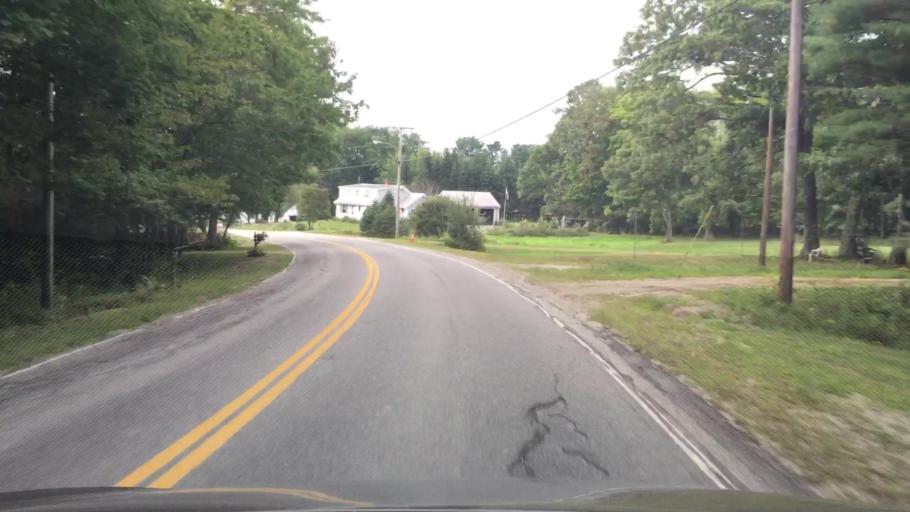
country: US
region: Maine
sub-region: Hancock County
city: Penobscot
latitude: 44.4601
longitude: -68.7055
